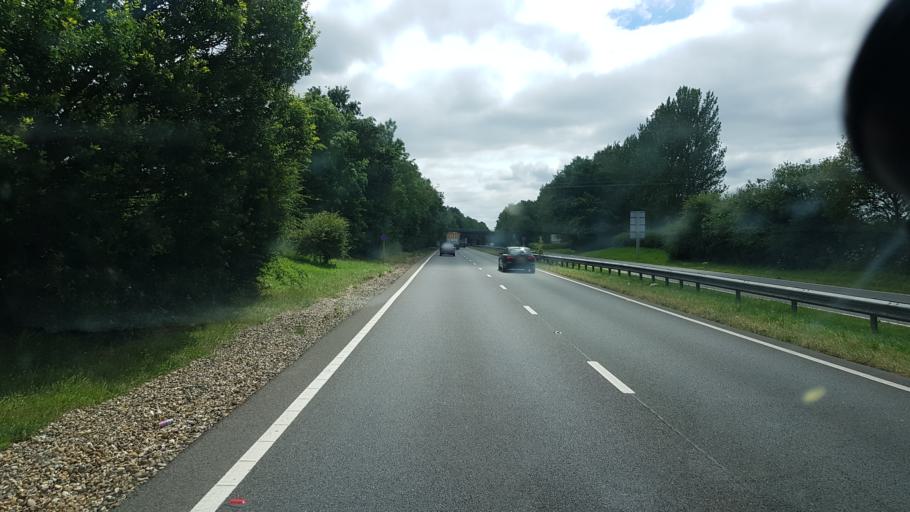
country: GB
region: England
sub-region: Surrey
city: Godstone
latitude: 51.2558
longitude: -0.0593
